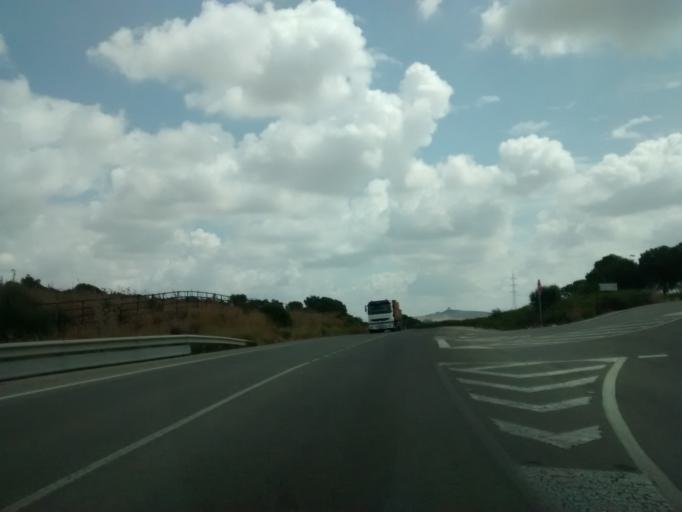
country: ES
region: Andalusia
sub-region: Provincia de Cadiz
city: Medina Sidonia
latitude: 36.4441
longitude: -5.8995
